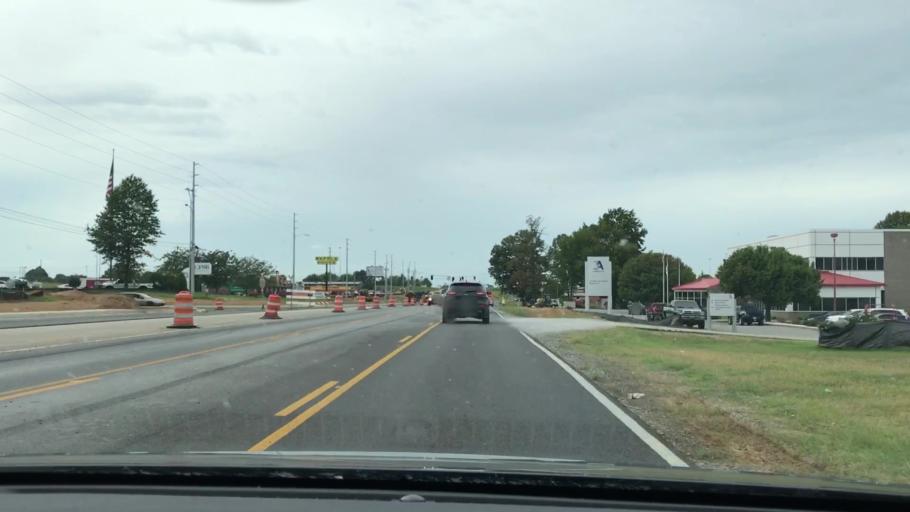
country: US
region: Kentucky
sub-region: Marshall County
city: Benton
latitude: 36.8663
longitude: -88.3576
